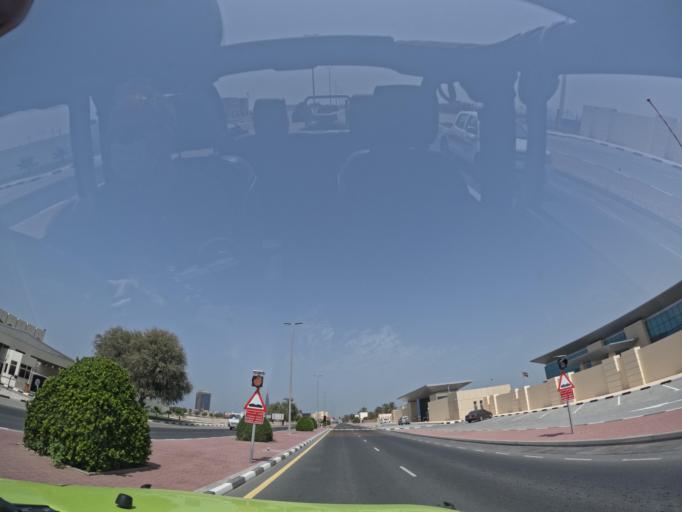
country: AE
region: Umm al Qaywayn
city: Umm al Qaywayn
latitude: 25.5701
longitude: 55.5654
